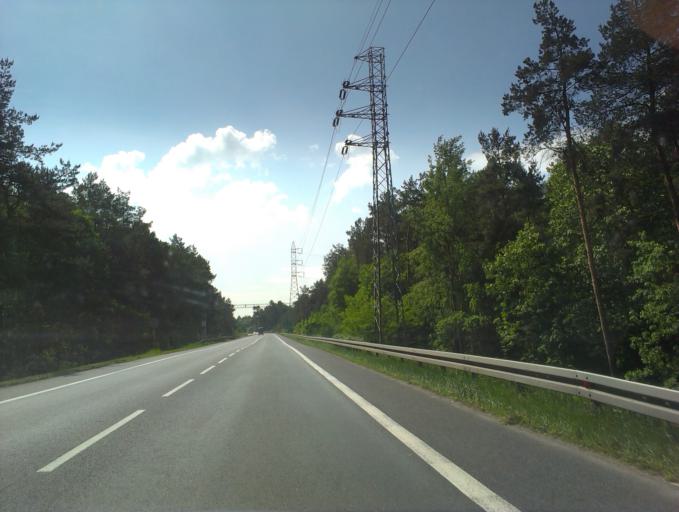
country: PL
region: Greater Poland Voivodeship
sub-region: Powiat pilski
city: Pila
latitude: 53.1542
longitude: 16.7881
